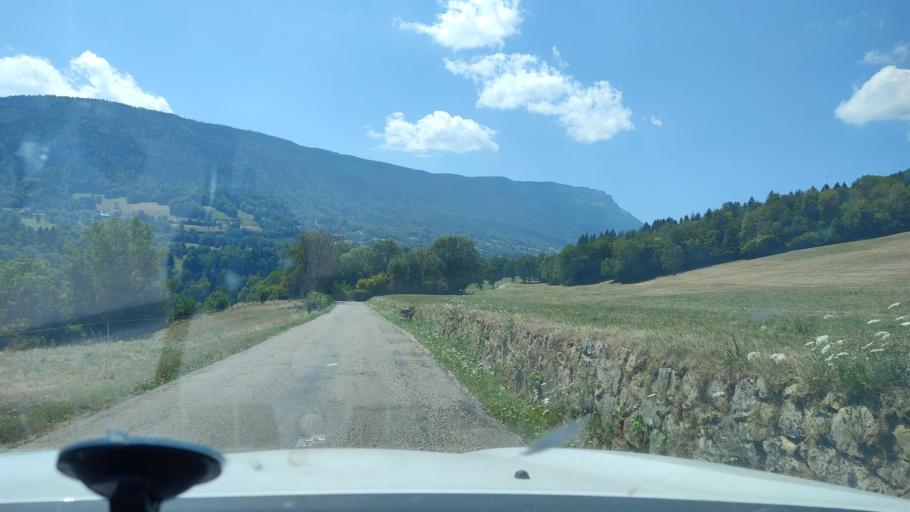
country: FR
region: Rhone-Alpes
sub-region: Departement de la Haute-Savoie
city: Cusy
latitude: 45.7077
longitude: 6.0806
